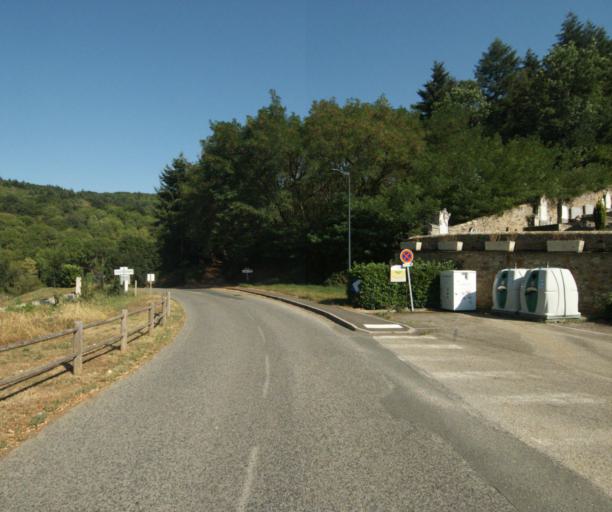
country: FR
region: Rhone-Alpes
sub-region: Departement du Rhone
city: Saint-Pierre-la-Palud
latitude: 45.7685
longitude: 4.6097
